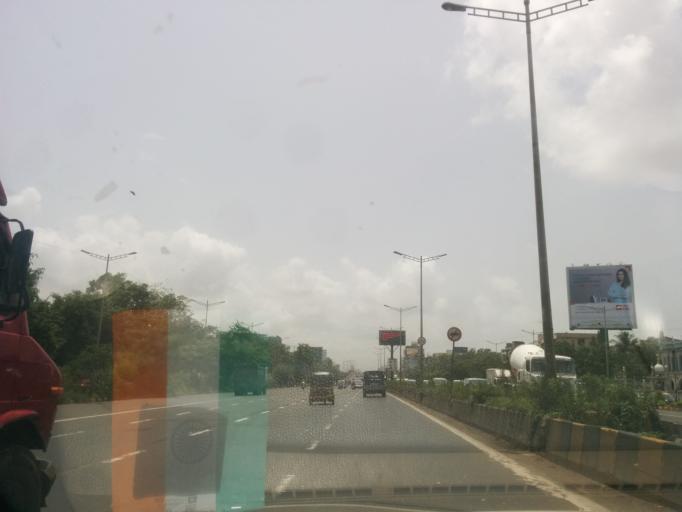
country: IN
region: Maharashtra
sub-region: Mumbai Suburban
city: Mumbai
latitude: 19.0651
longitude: 72.8466
